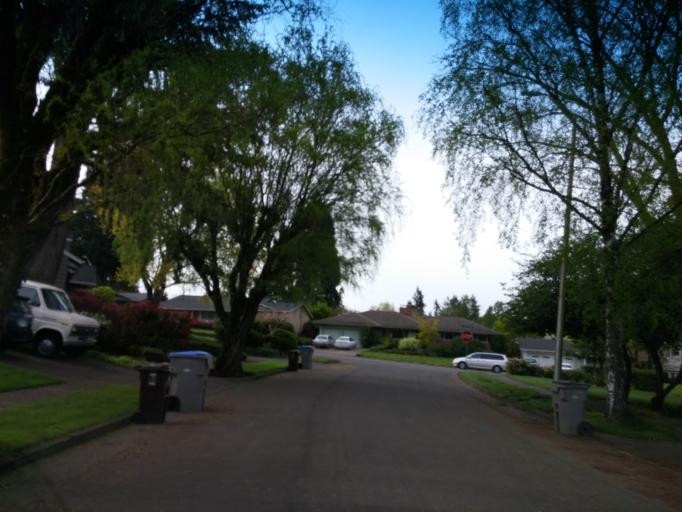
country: US
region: Oregon
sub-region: Washington County
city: Cedar Hills
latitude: 45.5096
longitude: -122.8085
